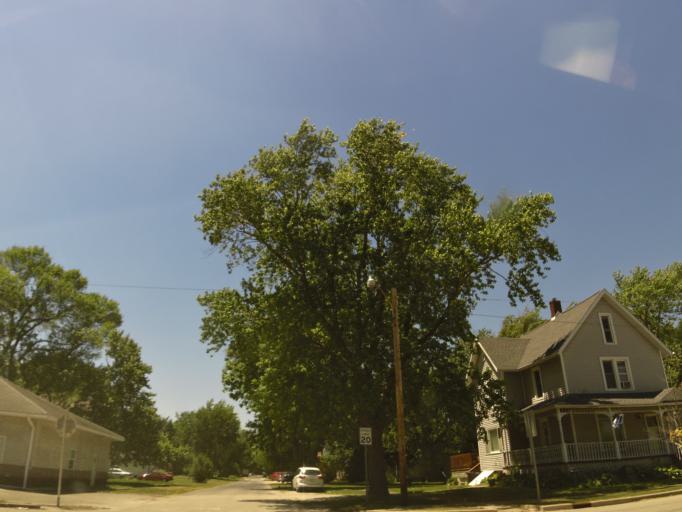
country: US
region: Illinois
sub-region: Livingston County
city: Chatsworth
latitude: 40.7571
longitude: -88.1901
